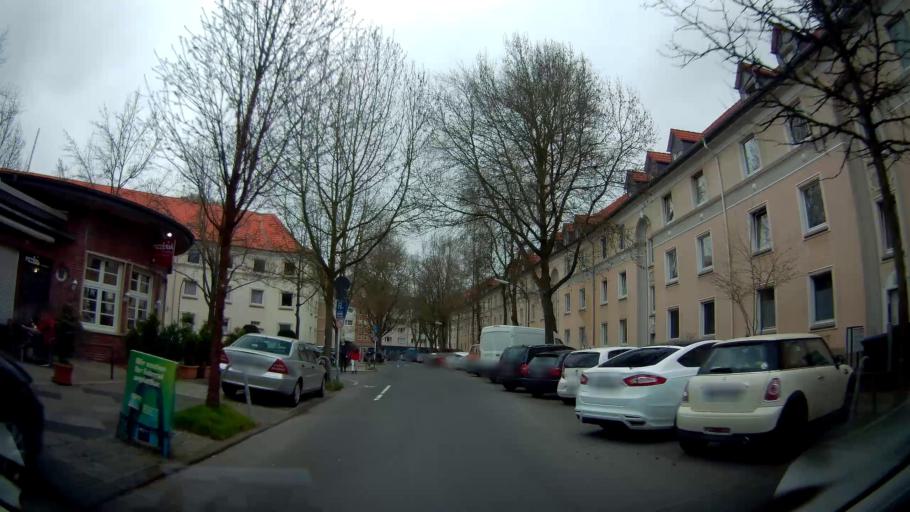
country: DE
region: North Rhine-Westphalia
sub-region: Regierungsbezirk Arnsberg
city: Dortmund
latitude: 51.5090
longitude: 7.4866
